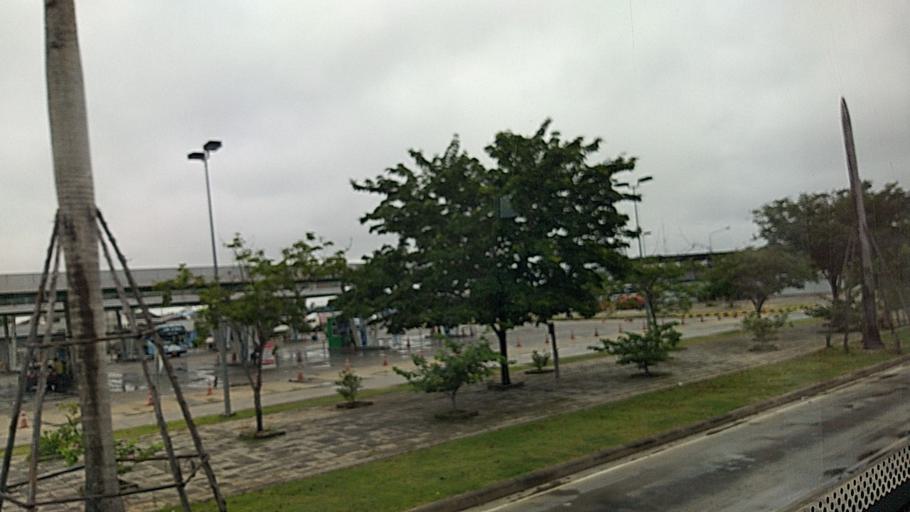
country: TH
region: Nakhon Ratchasima
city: Nakhon Ratchasima
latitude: 14.9923
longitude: 102.0925
